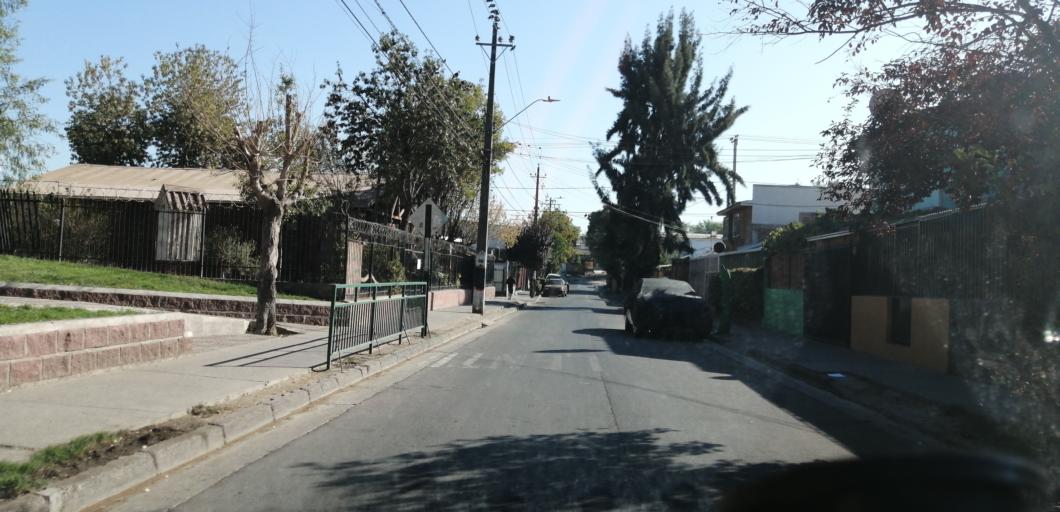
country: CL
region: Santiago Metropolitan
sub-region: Provincia de Santiago
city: Lo Prado
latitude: -33.4291
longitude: -70.7536
